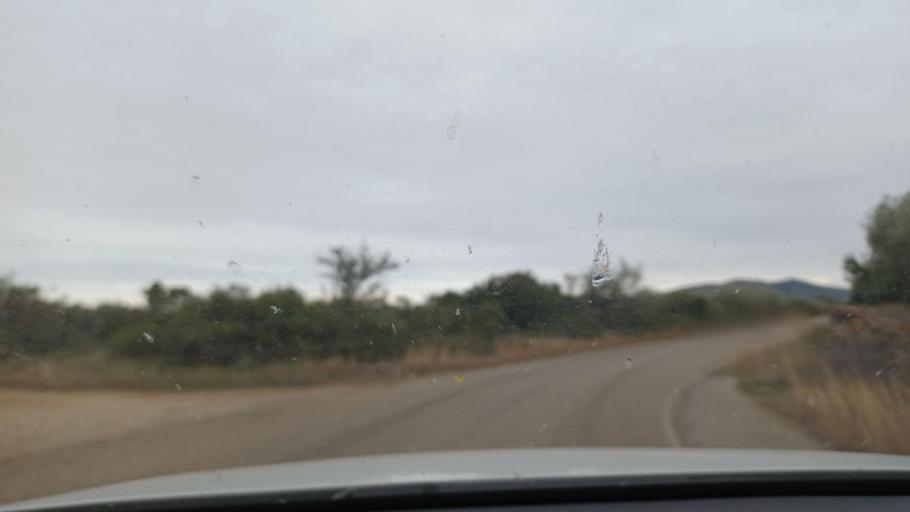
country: ES
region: Valencia
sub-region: Provincia de Castello
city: Canet lo Roig
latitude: 40.5863
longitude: 0.2856
